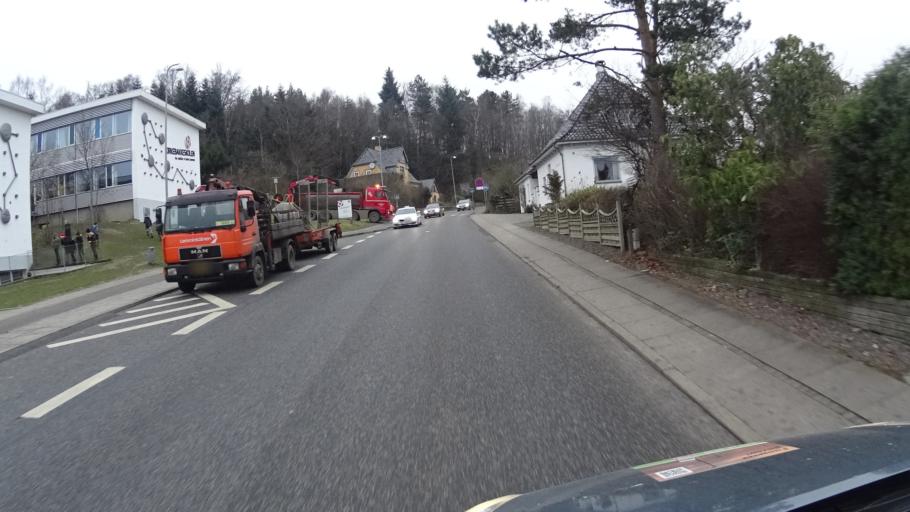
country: DK
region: South Denmark
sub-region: Vejle Kommune
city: Vejle
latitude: 55.7115
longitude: 9.6054
